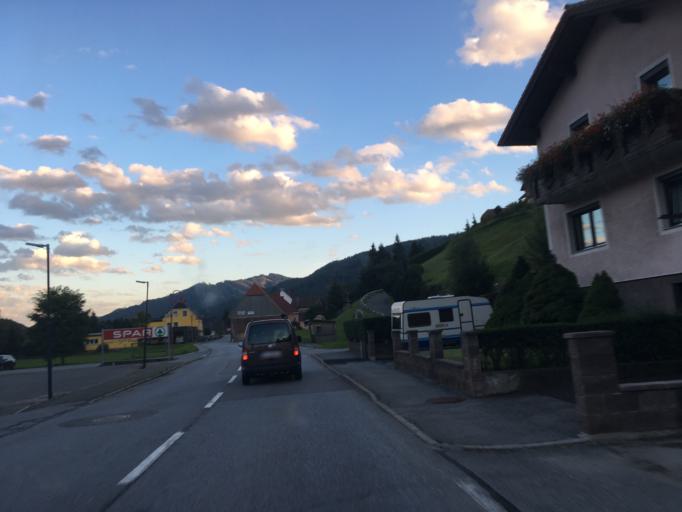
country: AT
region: Styria
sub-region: Politischer Bezirk Murtal
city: Oberzeiring
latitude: 47.2808
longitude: 14.4804
